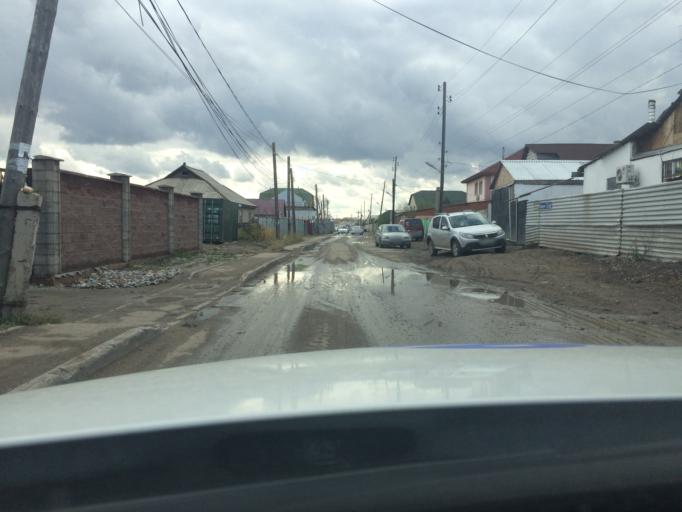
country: KZ
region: Astana Qalasy
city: Astana
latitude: 51.1854
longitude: 71.3979
